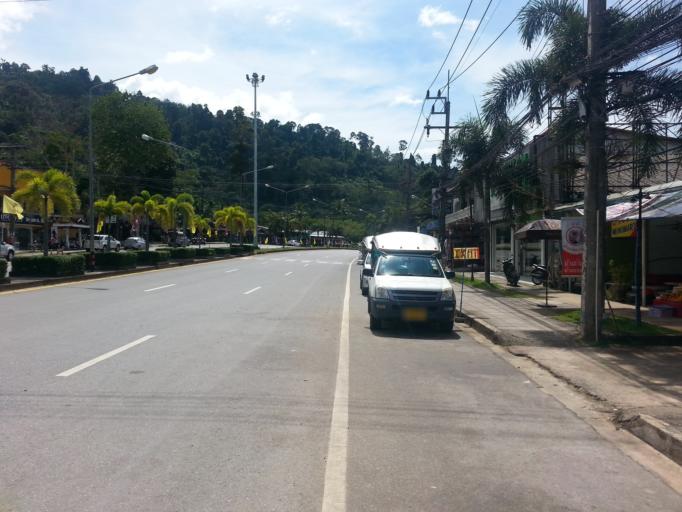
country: TH
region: Phangnga
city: Ban Khao Lak
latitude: 8.6418
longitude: 98.2508
